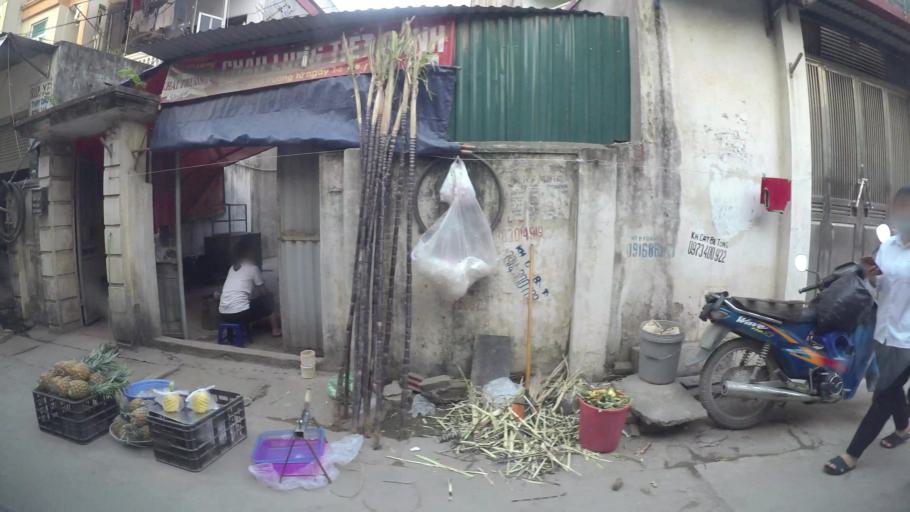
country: VN
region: Ha Noi
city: Ha Dong
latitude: 20.9959
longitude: 105.7298
